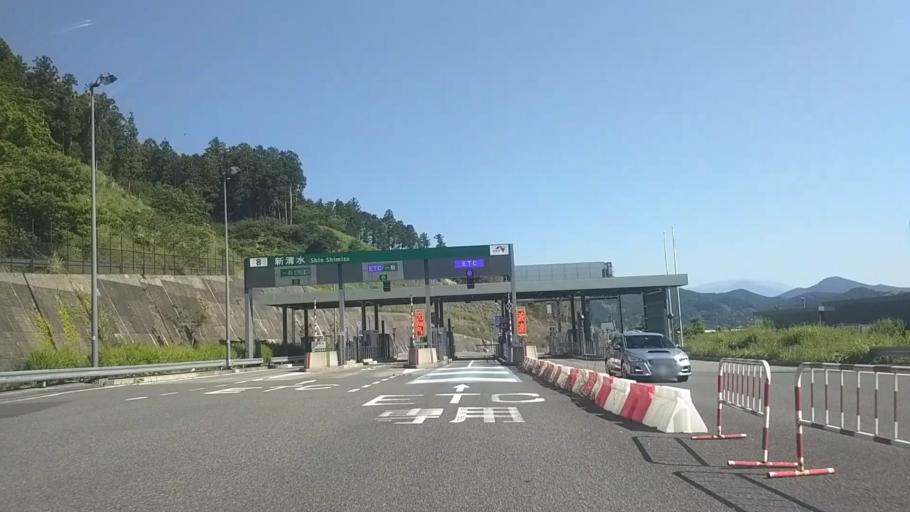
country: JP
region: Shizuoka
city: Fujinomiya
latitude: 35.1490
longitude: 138.5206
